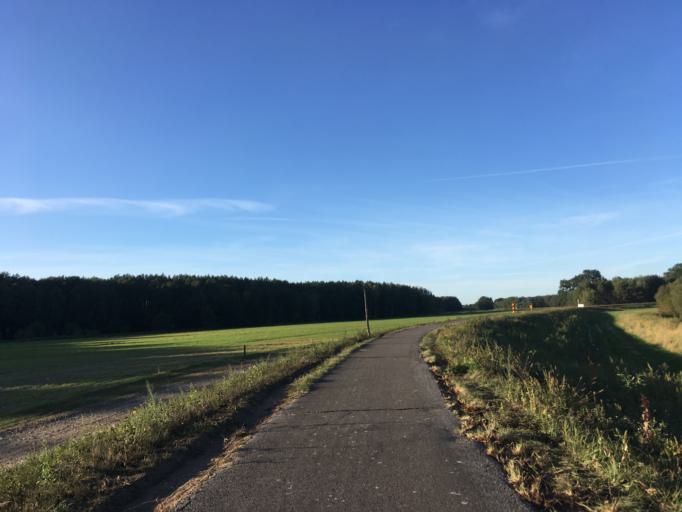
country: PL
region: Lubusz
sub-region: Powiat zarski
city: Trzebiel
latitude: 51.6517
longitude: 14.7505
